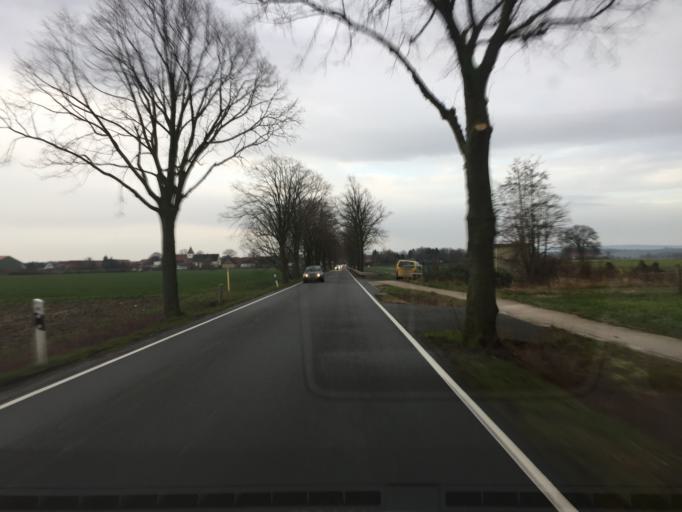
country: DE
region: Lower Saxony
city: Seelze
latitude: 52.3736
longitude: 9.5667
